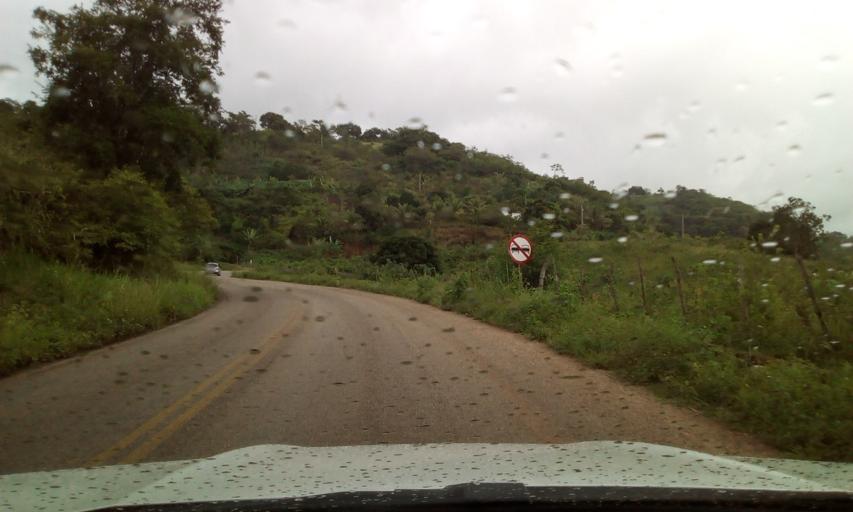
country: BR
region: Paraiba
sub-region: Areia
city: Areia
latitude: -6.8863
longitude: -35.6464
